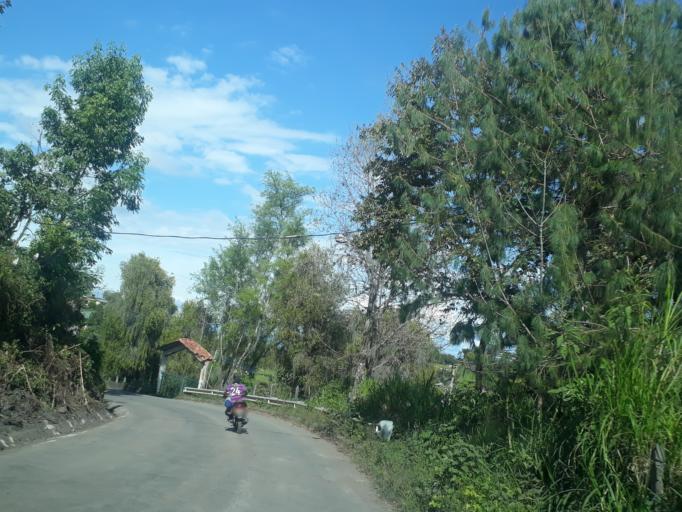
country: CO
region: Santander
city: Velez
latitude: 6.0246
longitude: -73.6570
